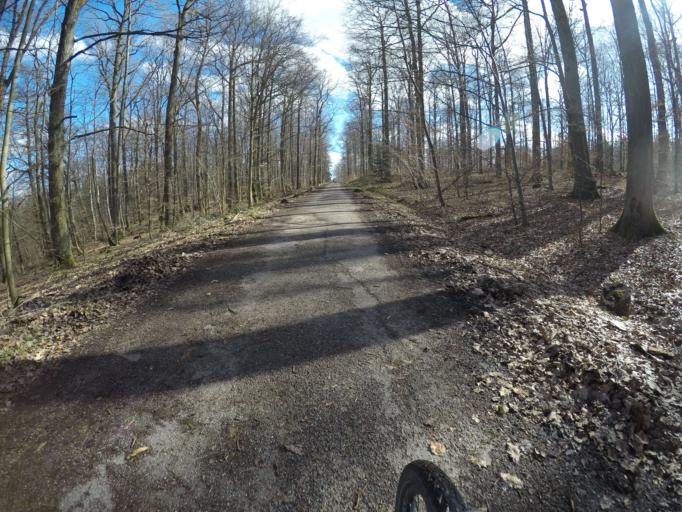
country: DE
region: Baden-Wuerttemberg
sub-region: Regierungsbezirk Stuttgart
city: Leinfelden-Echterdingen
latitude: 48.6838
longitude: 9.1434
